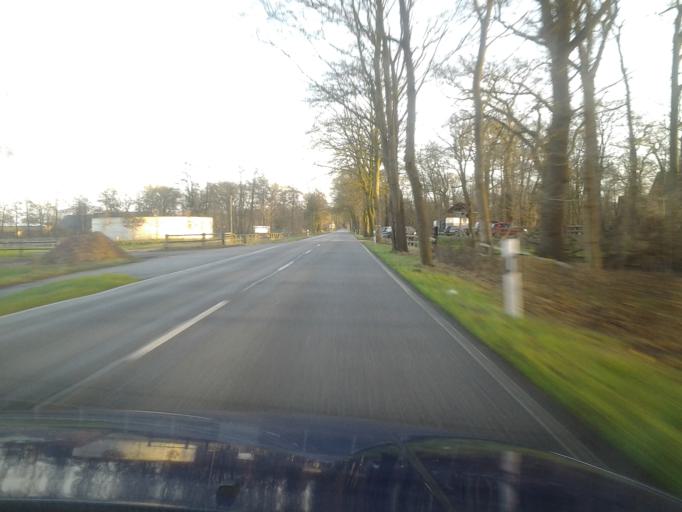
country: DE
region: Lower Saxony
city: Lilienthal
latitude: 53.1795
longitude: 8.8800
